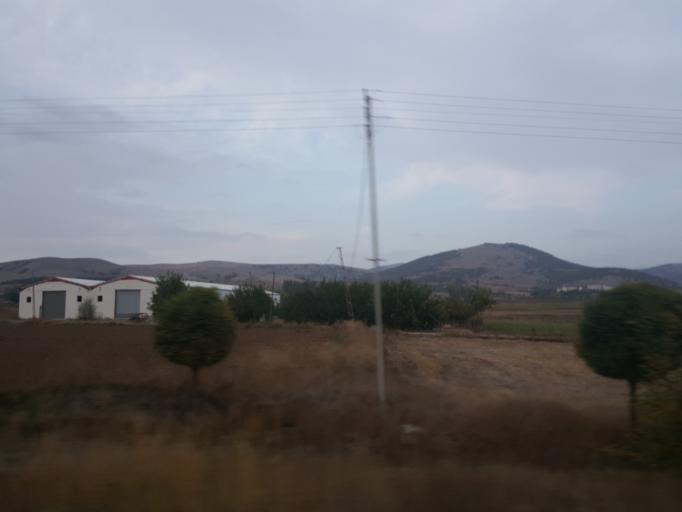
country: TR
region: Amasya
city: Gumushacikoy
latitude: 40.8872
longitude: 35.2056
